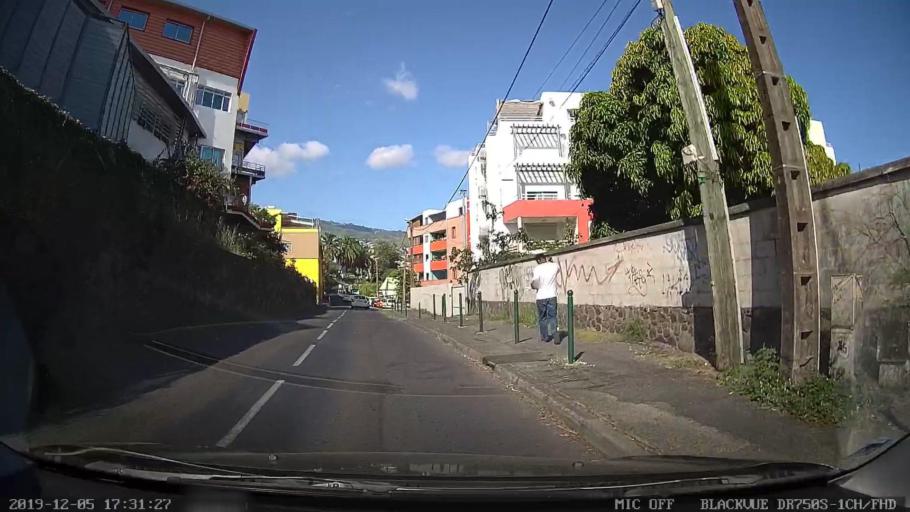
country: RE
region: Reunion
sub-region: Reunion
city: Saint-Denis
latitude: -20.9016
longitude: 55.4792
